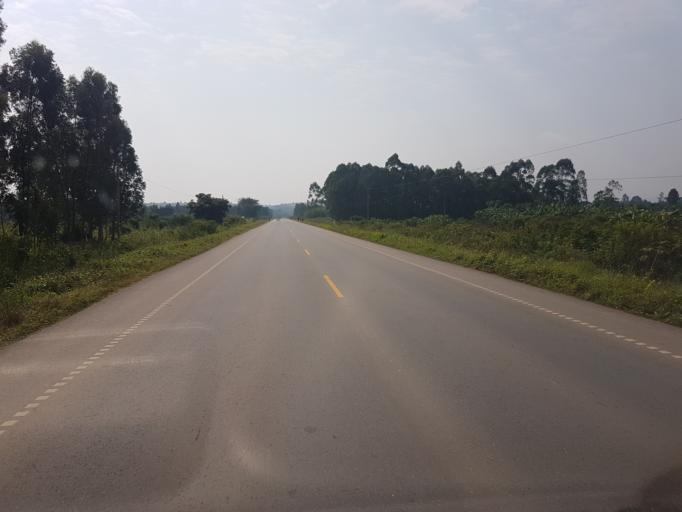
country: UG
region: Western Region
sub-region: Mbarara District
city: Bwizibwera
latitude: -0.6426
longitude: 30.5693
